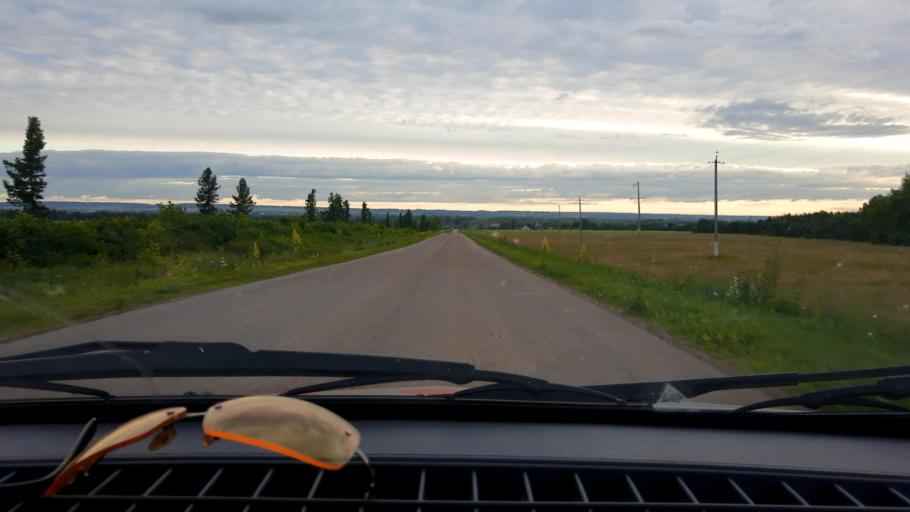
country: RU
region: Bashkortostan
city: Chishmy
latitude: 54.5413
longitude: 55.4685
